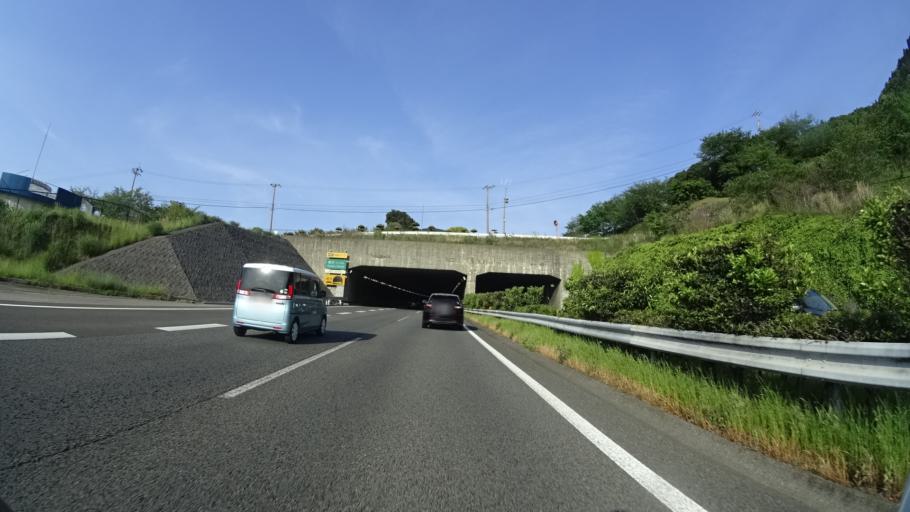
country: JP
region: Ehime
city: Niihama
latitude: 33.9309
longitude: 133.3503
